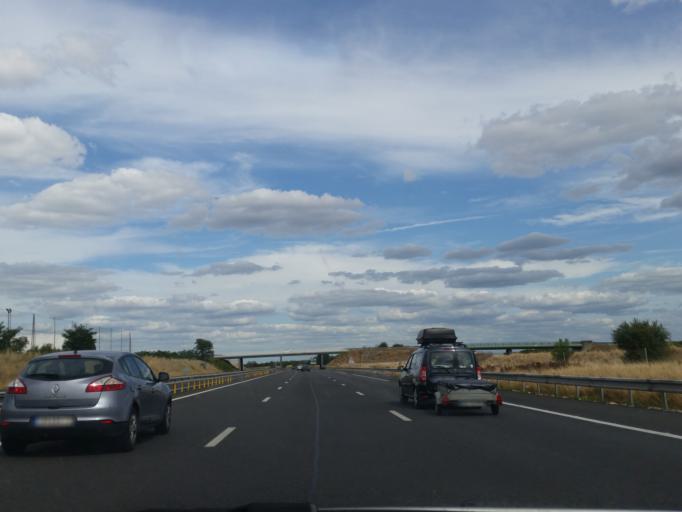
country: FR
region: Centre
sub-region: Departement du Loir-et-Cher
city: Villebarou
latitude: 47.6174
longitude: 1.3235
